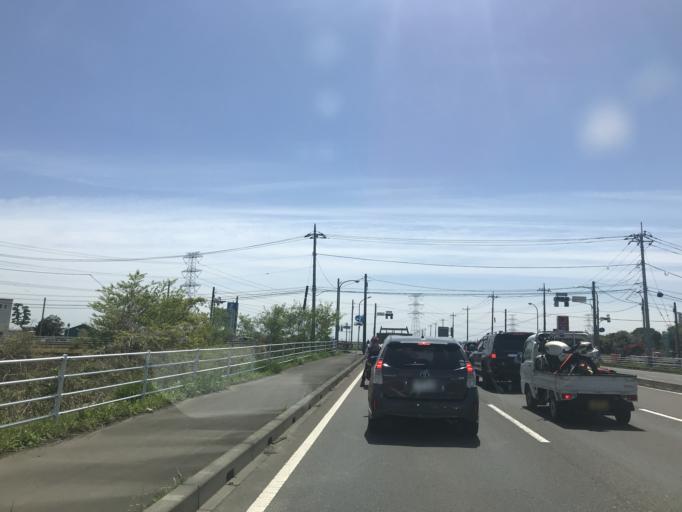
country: JP
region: Ibaraki
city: Shimodate
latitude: 36.2498
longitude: 139.9833
